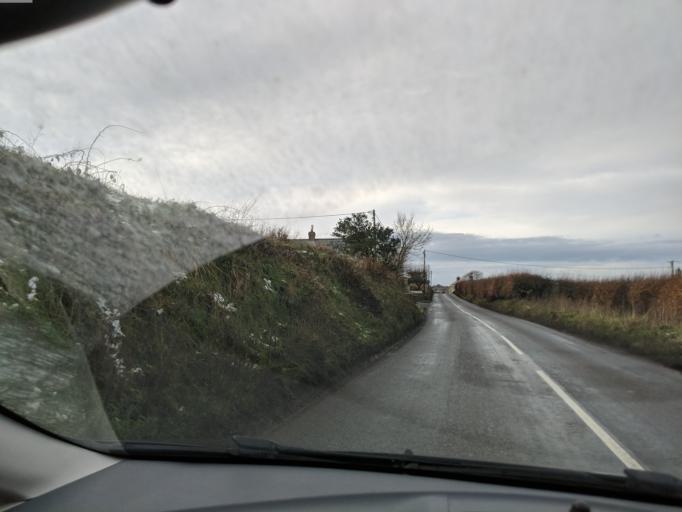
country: GB
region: England
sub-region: Cornwall
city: Jacobstow
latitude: 50.6627
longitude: -4.5802
